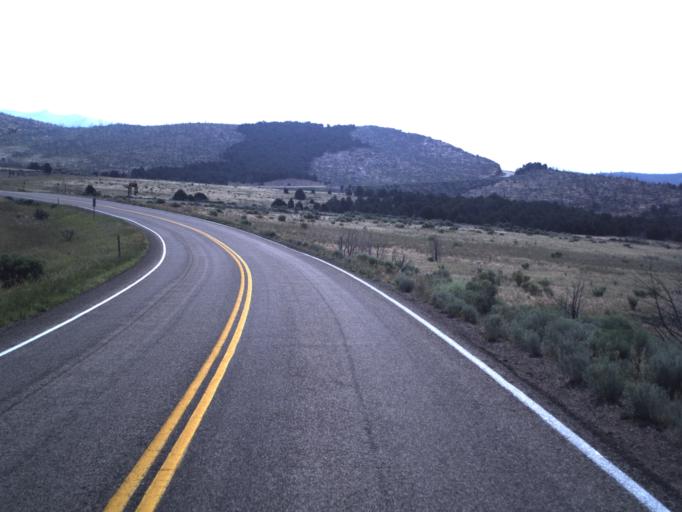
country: US
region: Utah
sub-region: Daggett County
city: Manila
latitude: 40.9451
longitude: -109.4349
